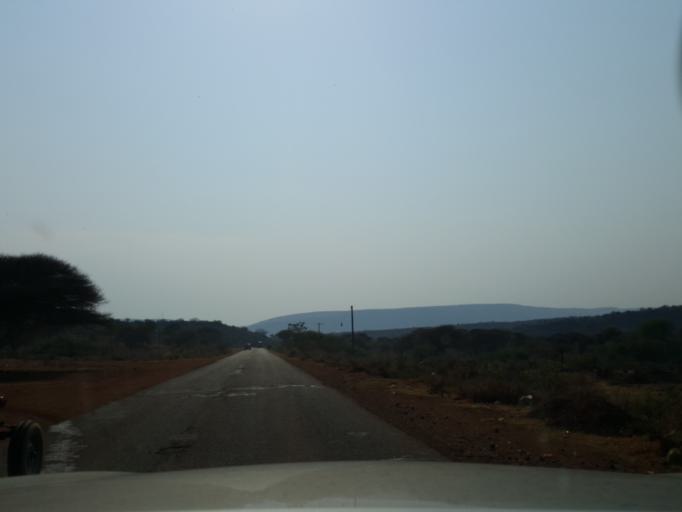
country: BW
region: South East
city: Lobatse
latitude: -25.3053
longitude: 25.8192
